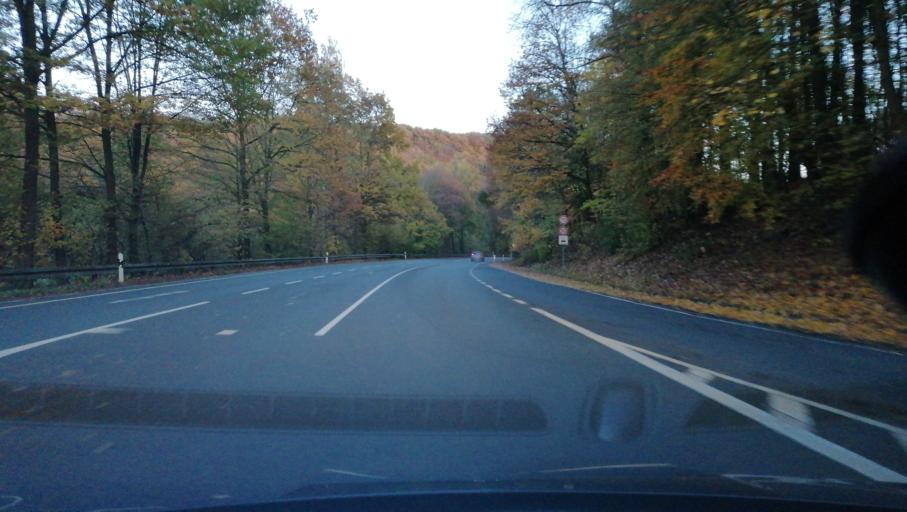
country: DE
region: North Rhine-Westphalia
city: Herdecke
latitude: 51.4146
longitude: 7.4225
